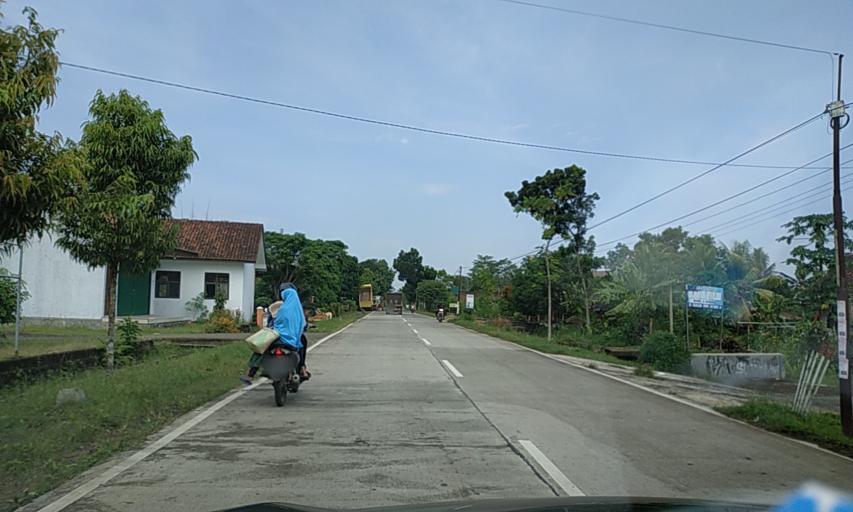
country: ID
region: Central Java
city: Tambangan
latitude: -7.4838
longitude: 108.8231
